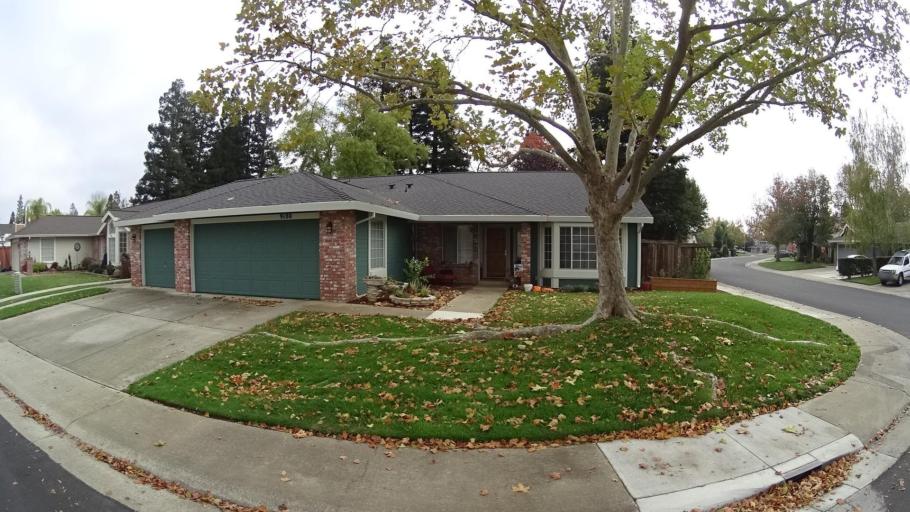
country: US
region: California
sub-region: Sacramento County
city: Elk Grove
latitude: 38.4215
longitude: -121.3595
